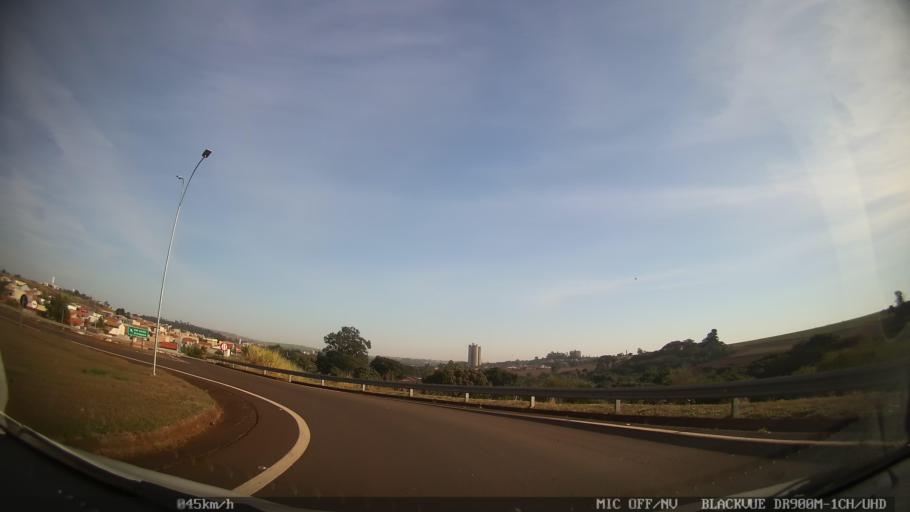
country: BR
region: Sao Paulo
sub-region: Cravinhos
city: Cravinhos
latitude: -21.2776
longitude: -47.8044
